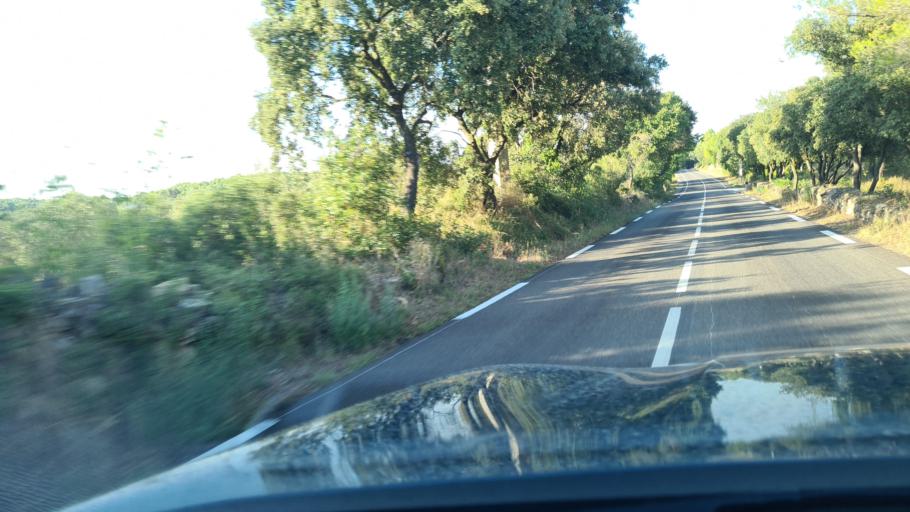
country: FR
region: Provence-Alpes-Cote d'Azur
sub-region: Departement des Bouches-du-Rhone
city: Cornillon-Confoux
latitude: 43.5713
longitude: 5.0751
